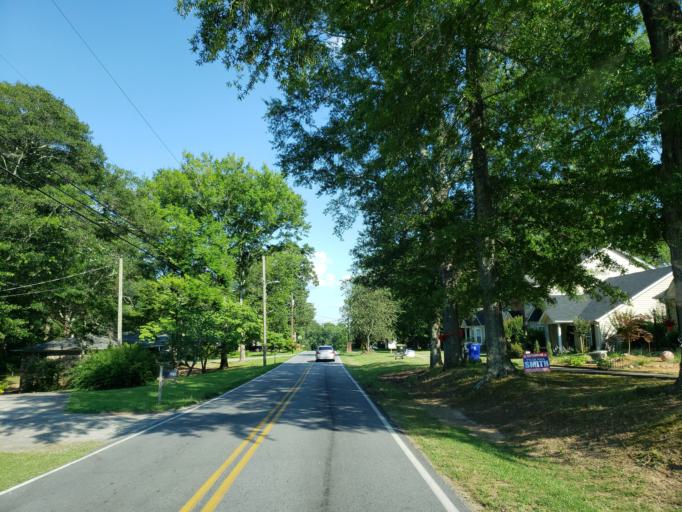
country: US
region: Georgia
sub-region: Haralson County
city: Bremen
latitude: 33.7161
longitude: -85.1383
